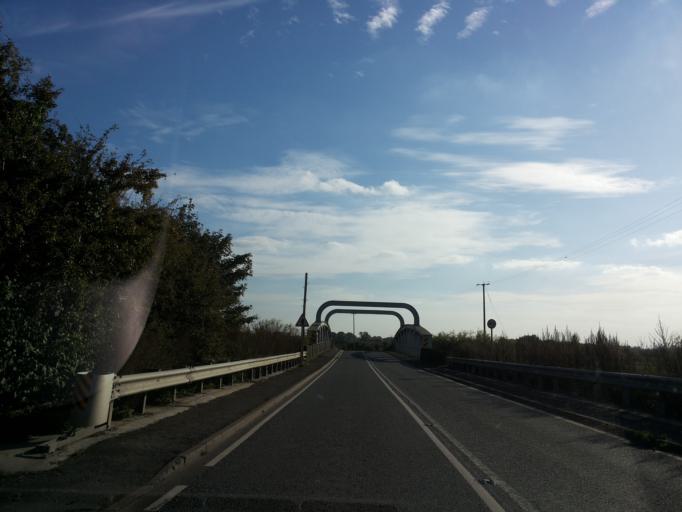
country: GB
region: England
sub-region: East Riding of Yorkshire
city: Rawcliffe
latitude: 53.6746
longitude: -0.9902
